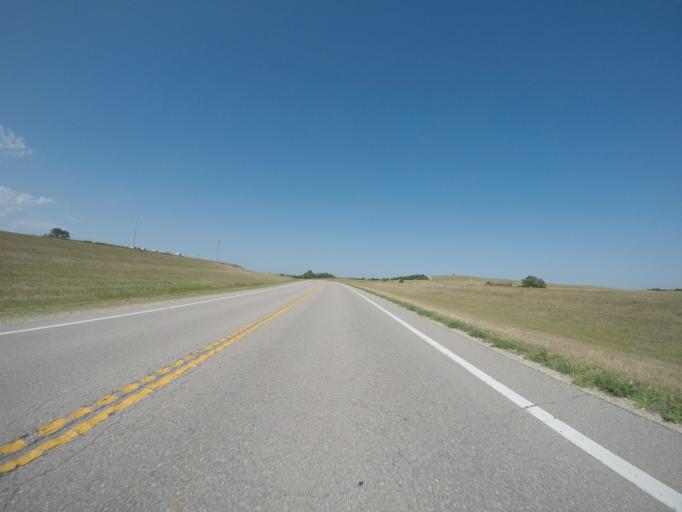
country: US
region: Kansas
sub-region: Clay County
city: Clay Center
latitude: 39.3781
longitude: -97.3864
